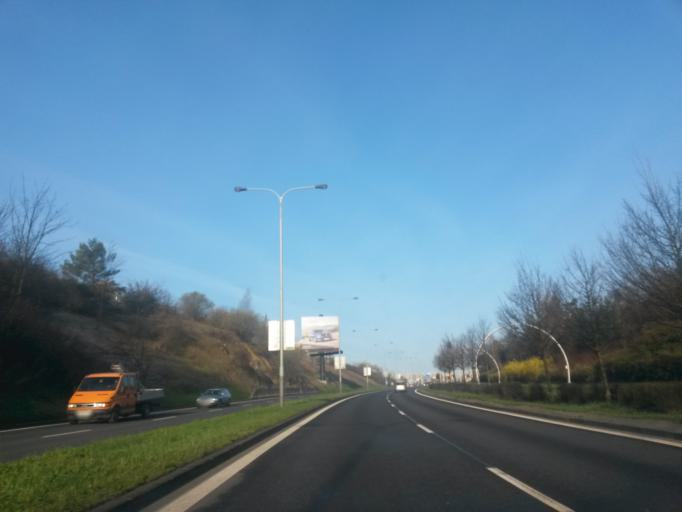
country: CZ
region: Praha
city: Branik
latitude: 50.0357
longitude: 14.3933
